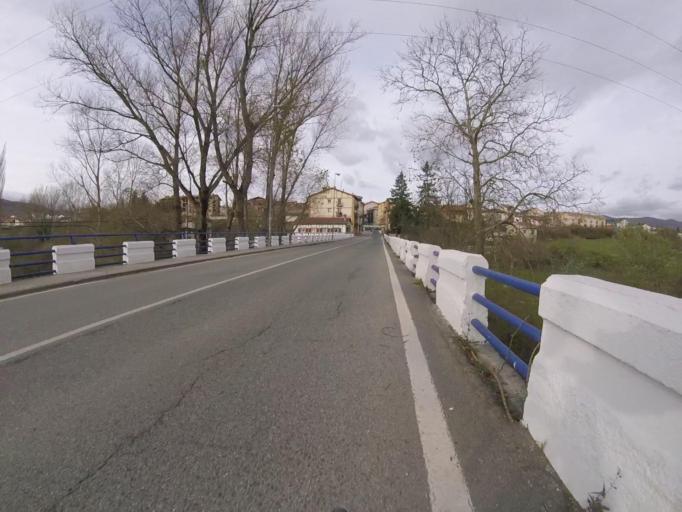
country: ES
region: Navarre
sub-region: Provincia de Navarra
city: Altsasu
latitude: 42.8922
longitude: -2.1665
